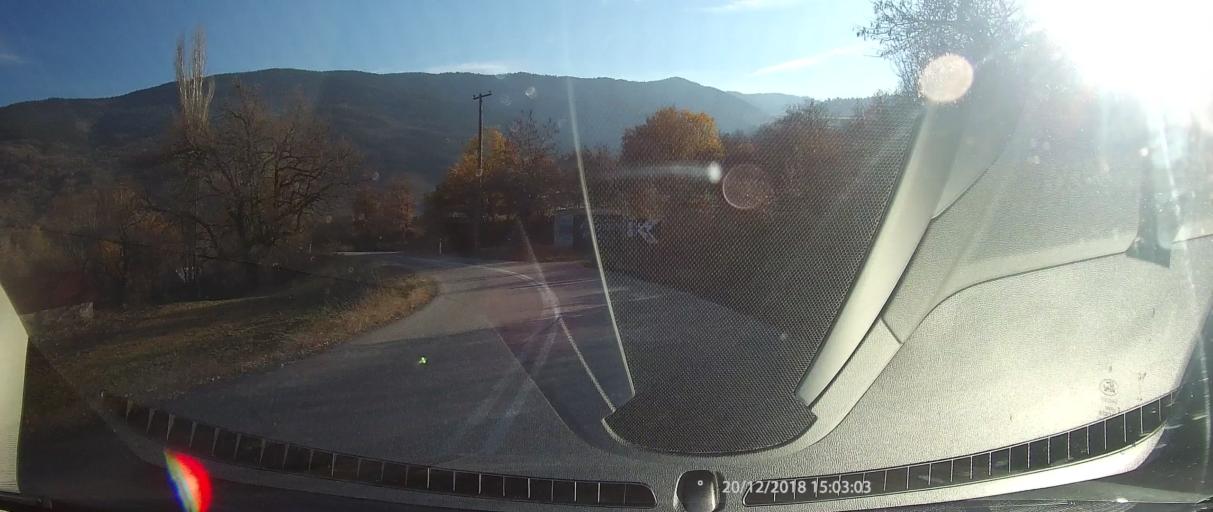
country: GR
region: Central Greece
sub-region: Nomos Evrytanias
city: Karpenisi
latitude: 38.9111
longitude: 21.9215
